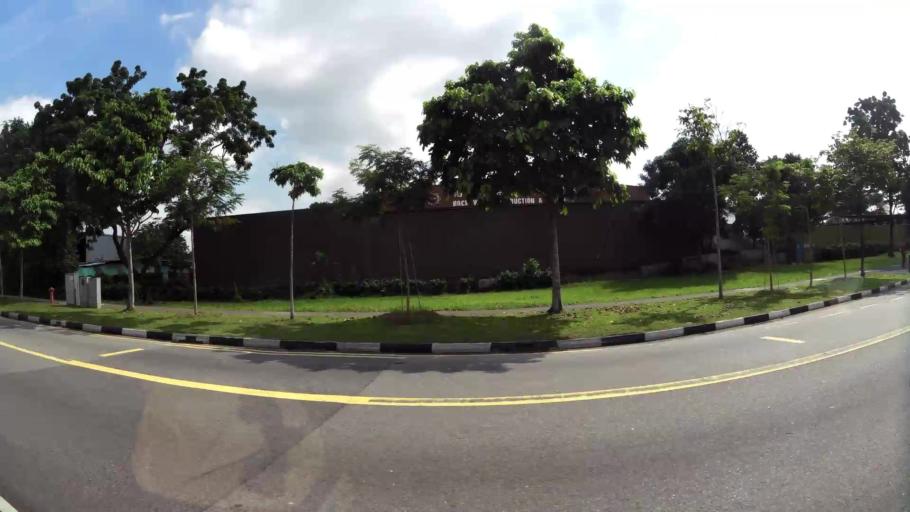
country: SG
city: Singapore
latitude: 1.3417
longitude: 103.8917
